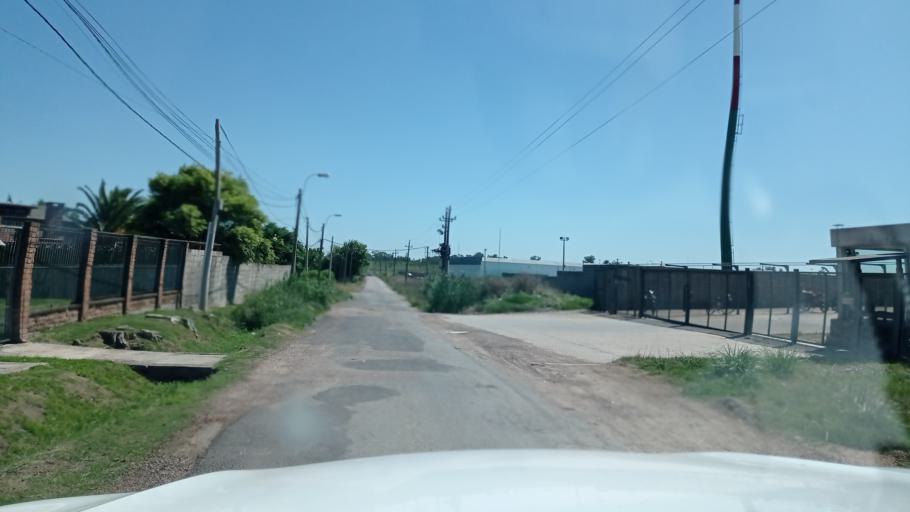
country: UY
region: Montevideo
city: Pajas Blancas
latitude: -34.8705
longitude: -56.2832
